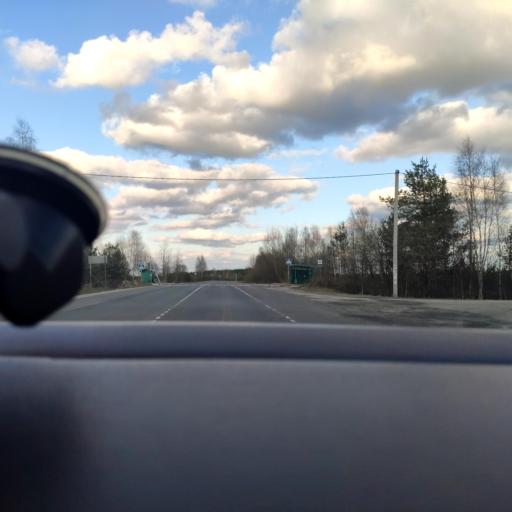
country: RU
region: Moskovskaya
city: Krasnyy Tkach
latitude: 55.4276
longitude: 39.2653
